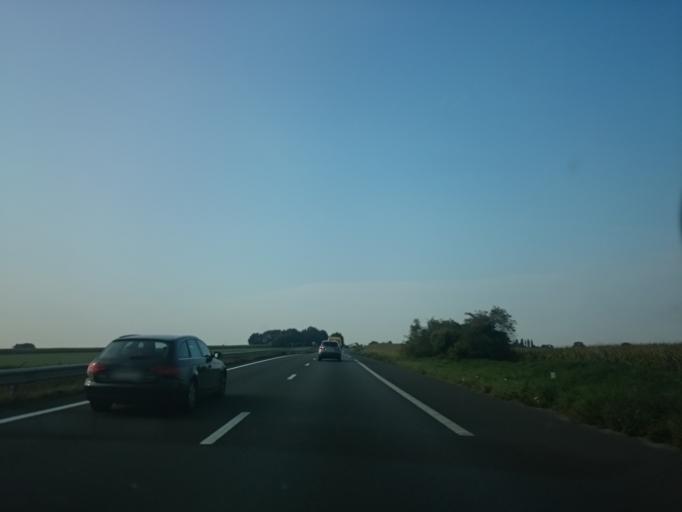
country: FR
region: Brittany
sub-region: Departement des Cotes-d'Armor
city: Plestan
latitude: 48.4386
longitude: -2.4742
